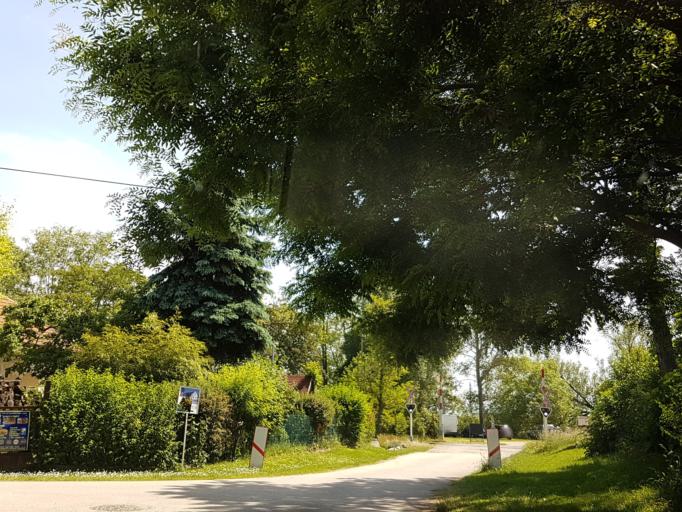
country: HU
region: Veszprem
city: Zanka
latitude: 46.8801
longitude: 17.7422
